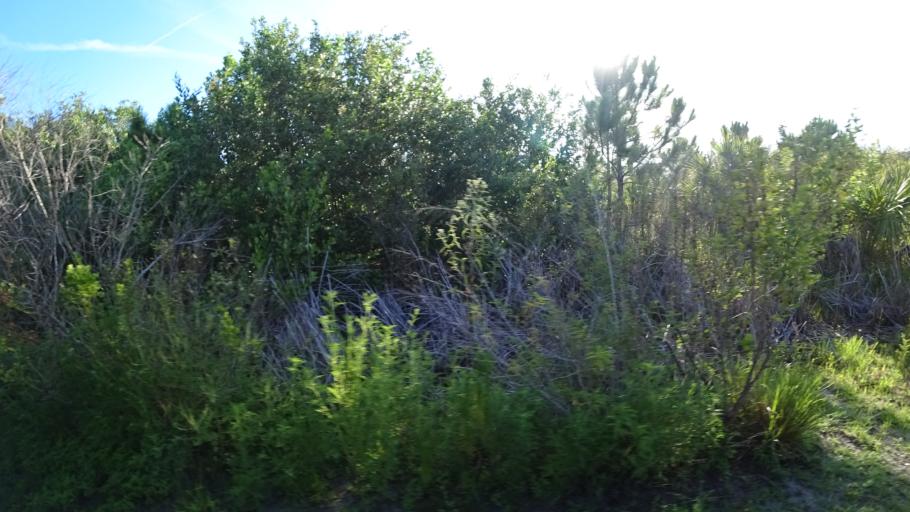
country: US
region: Florida
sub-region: Manatee County
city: Holmes Beach
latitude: 27.5140
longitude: -82.6675
